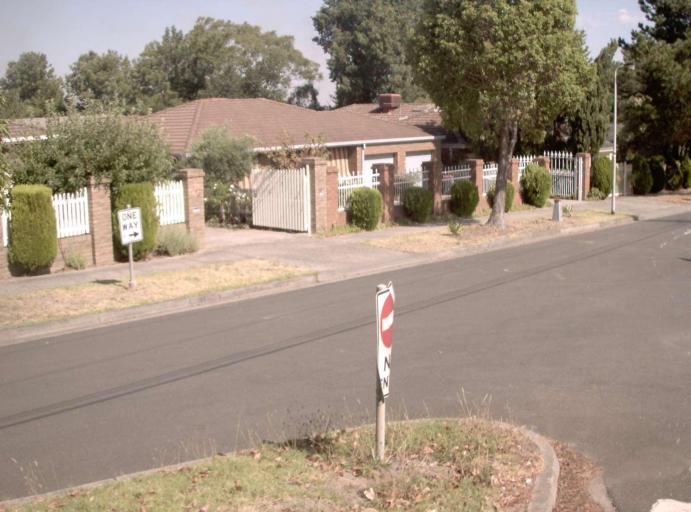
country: AU
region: Victoria
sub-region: Monash
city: Mulgrave
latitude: -37.9163
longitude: 145.1873
